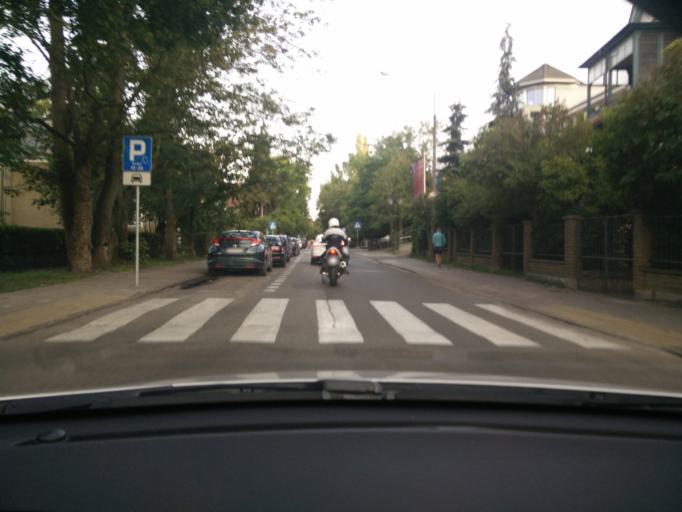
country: PL
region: Pomeranian Voivodeship
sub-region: Sopot
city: Sopot
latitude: 54.4513
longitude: 18.5615
